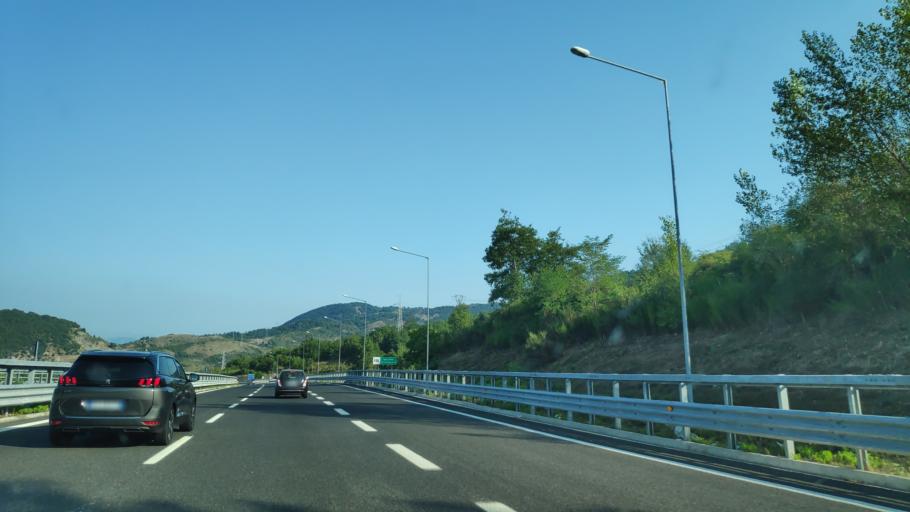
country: IT
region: Basilicate
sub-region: Provincia di Potenza
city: Lagonegro
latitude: 40.1504
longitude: 15.7504
